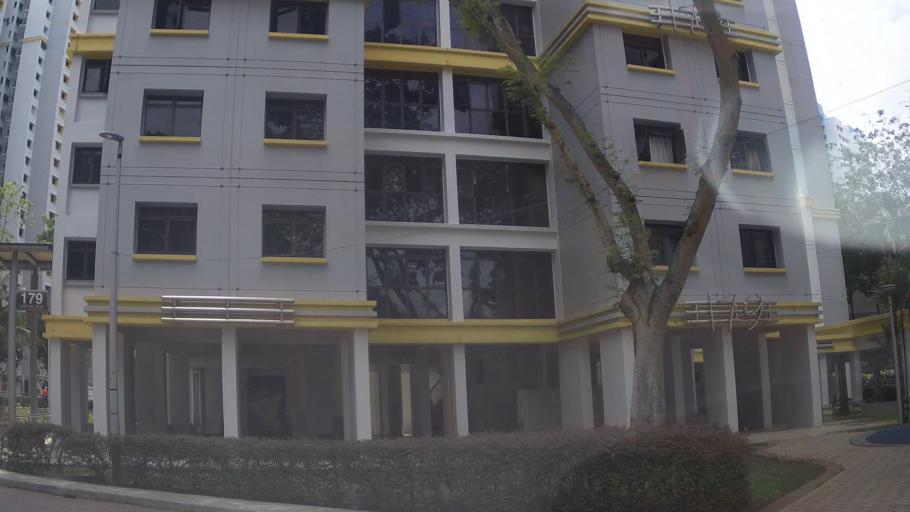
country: MY
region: Johor
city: Johor Bahru
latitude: 1.3798
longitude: 103.7654
